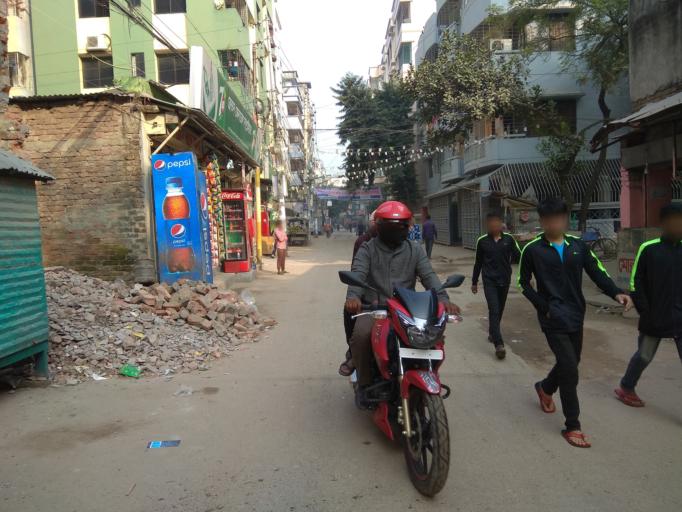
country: BD
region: Dhaka
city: Tungi
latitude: 23.8214
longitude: 90.3678
